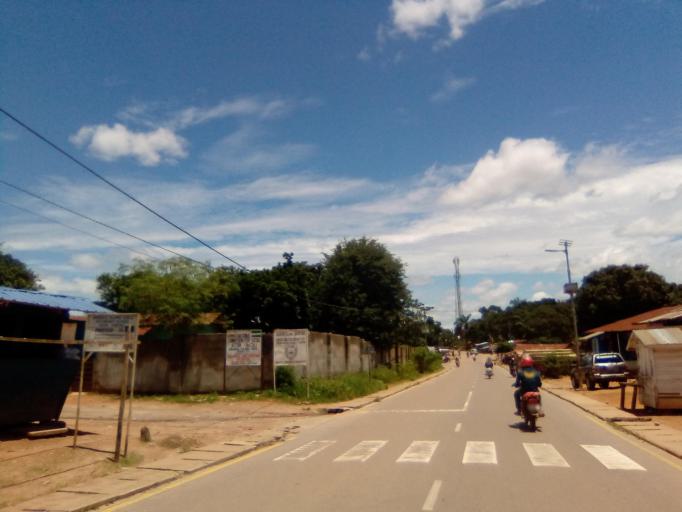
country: SL
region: Eastern Province
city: Koidu
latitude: 8.6386
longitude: -10.9710
